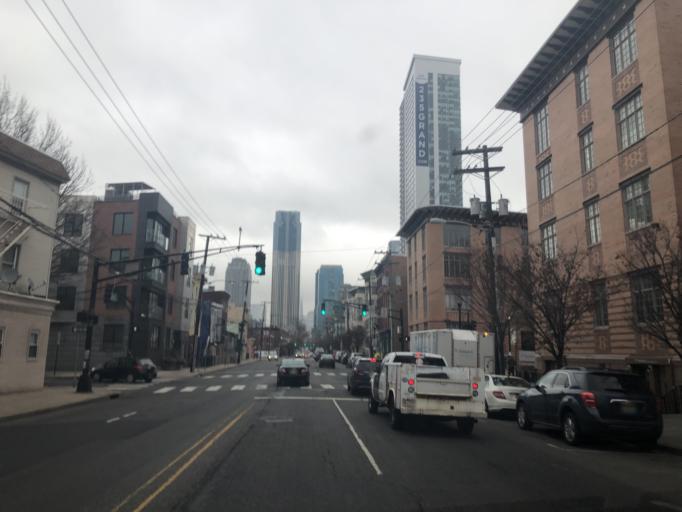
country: US
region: New Jersey
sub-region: Hudson County
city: Hoboken
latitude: 40.7164
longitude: -74.0477
